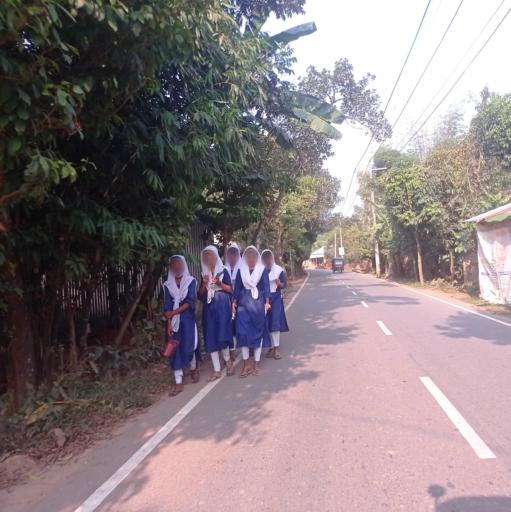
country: BD
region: Dhaka
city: Bhairab Bazar
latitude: 24.0610
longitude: 90.8401
